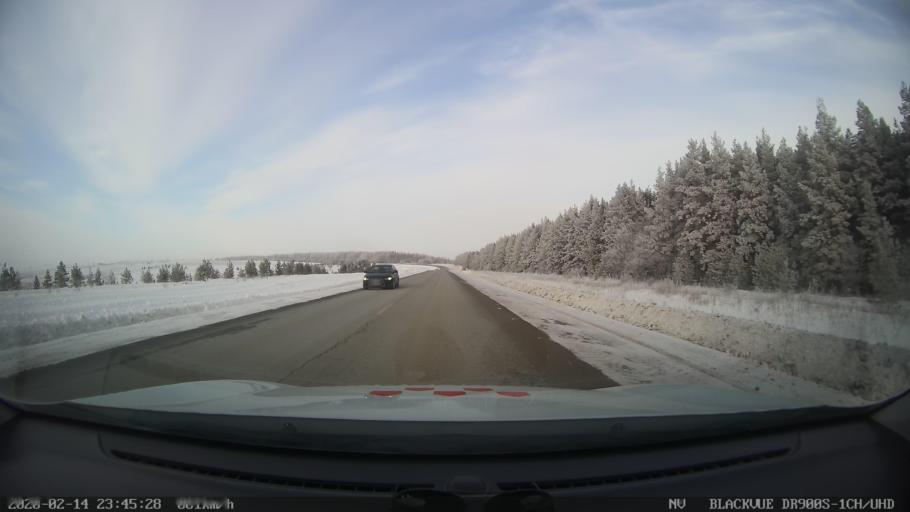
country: RU
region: Tatarstan
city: Kuybyshevskiy Zaton
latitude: 55.2213
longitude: 49.2323
